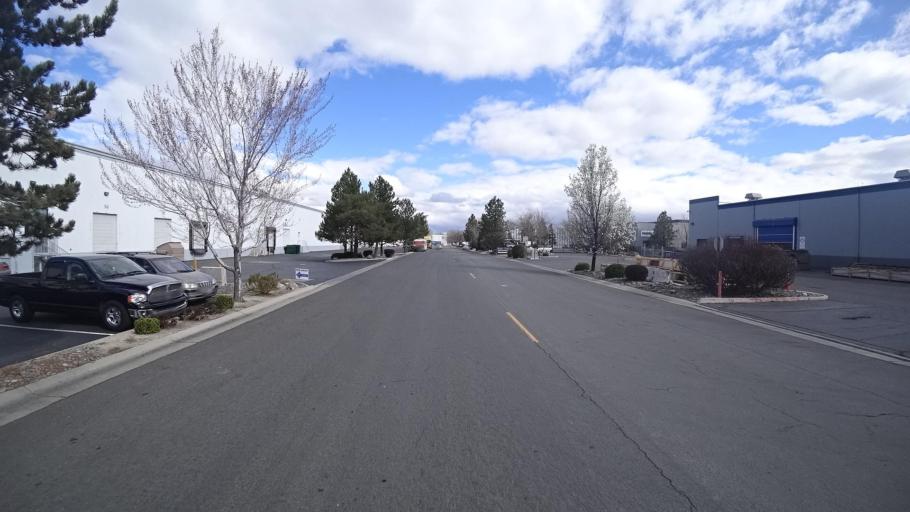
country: US
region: Nevada
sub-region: Washoe County
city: Sparks
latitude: 39.5219
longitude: -119.7263
